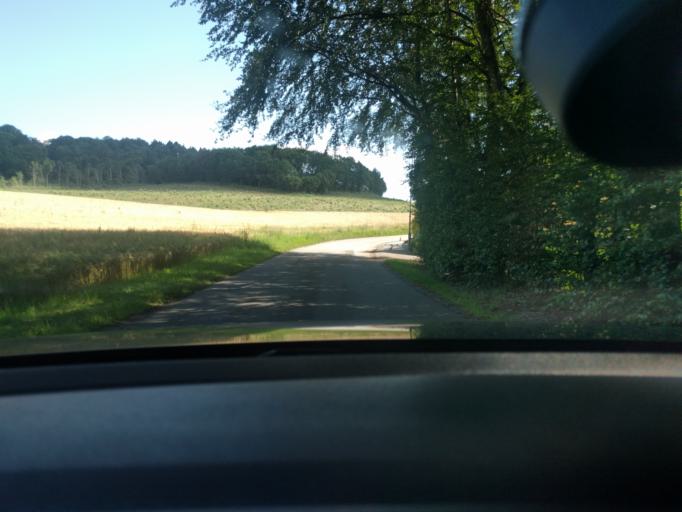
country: DK
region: Central Jutland
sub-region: Viborg Kommune
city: Viborg
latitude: 56.5138
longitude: 9.3101
